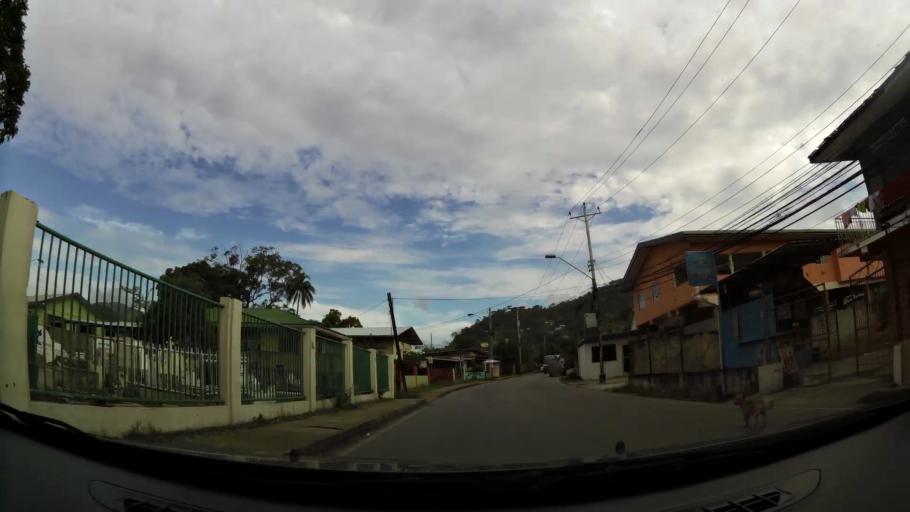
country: TT
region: San Juan/Laventille
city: Laventille
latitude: 10.6555
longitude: -61.4476
